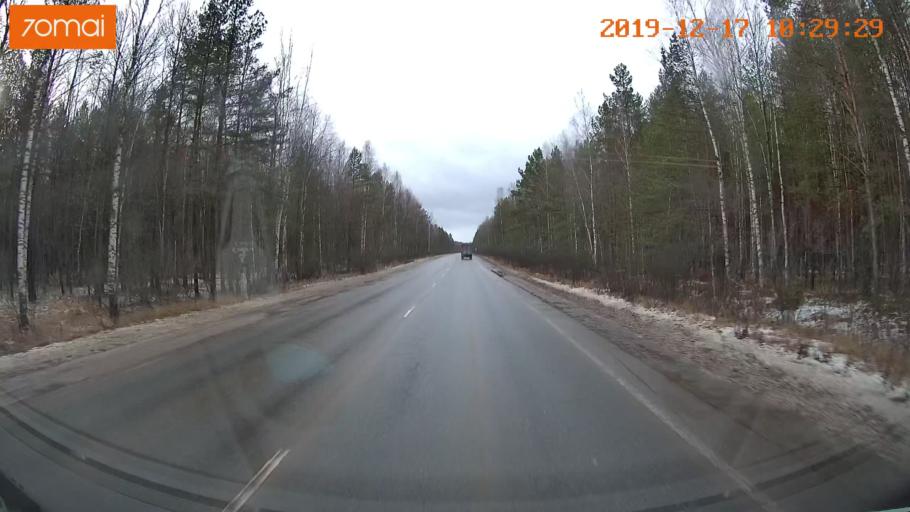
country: RU
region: Vladimir
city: Anopino
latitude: 55.6516
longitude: 40.7199
